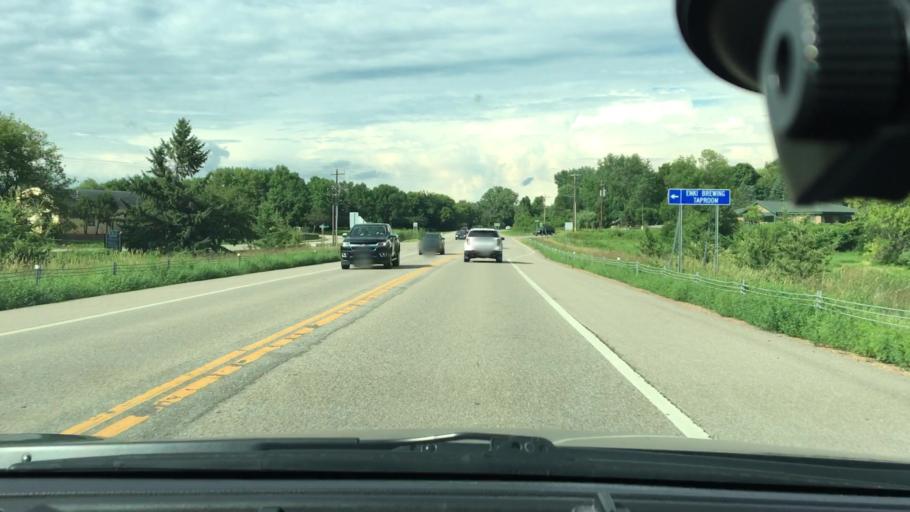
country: US
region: Minnesota
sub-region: Carver County
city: Victoria
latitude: 44.8618
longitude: -93.6546
